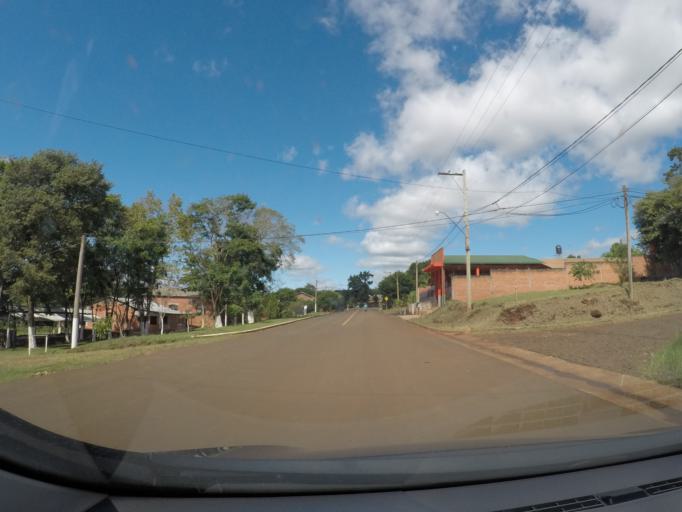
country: AR
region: Misiones
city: Puerto Rico
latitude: -26.8007
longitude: -55.0135
